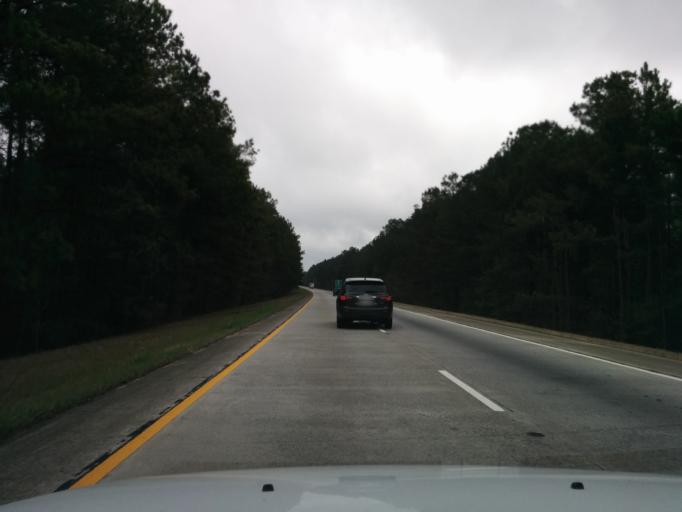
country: US
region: Georgia
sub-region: Candler County
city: Metter
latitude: 32.3775
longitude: -82.1952
